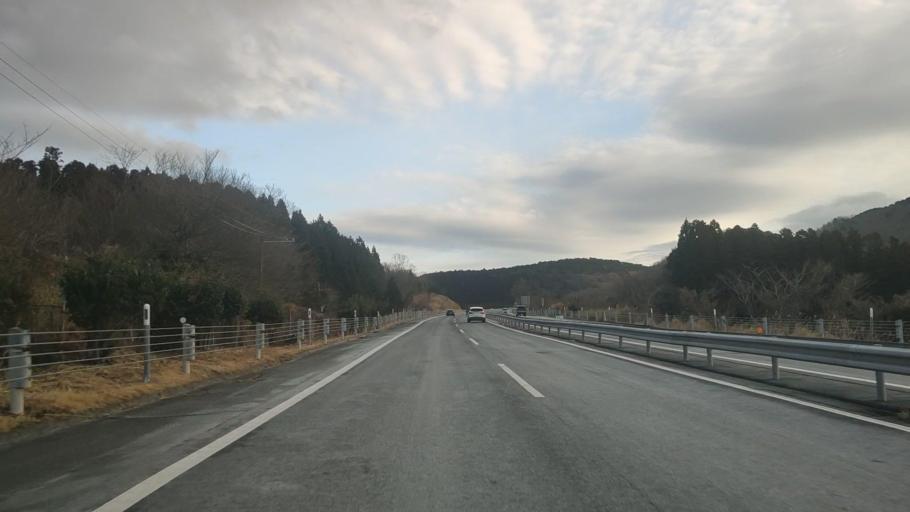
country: JP
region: Oita
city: Beppu
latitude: 33.2887
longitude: 131.3500
